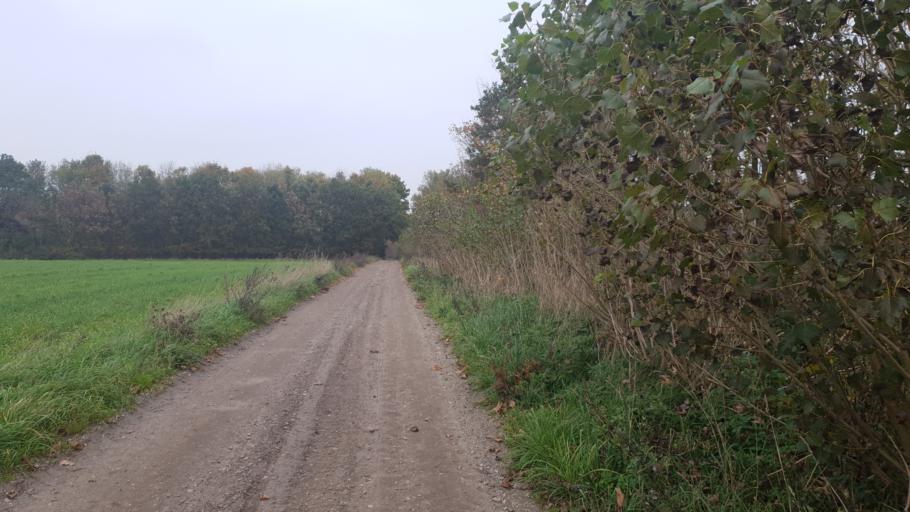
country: DK
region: Central Jutland
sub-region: Hedensted Kommune
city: Hedensted
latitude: 55.7946
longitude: 9.6820
